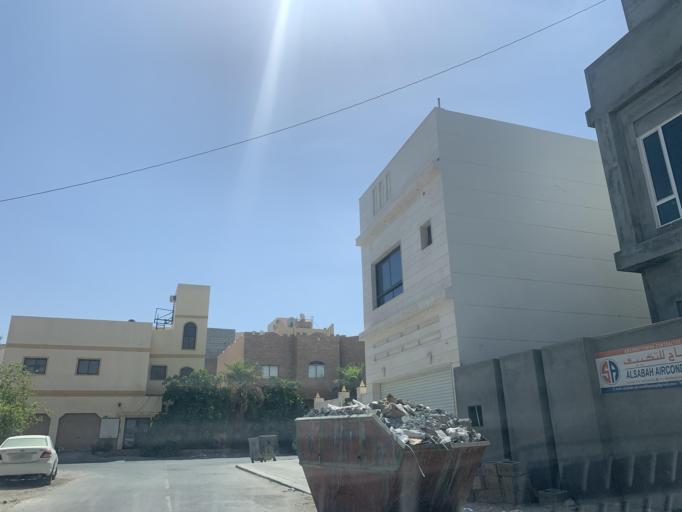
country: BH
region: Manama
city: Jidd Hafs
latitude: 26.2262
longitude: 50.5066
